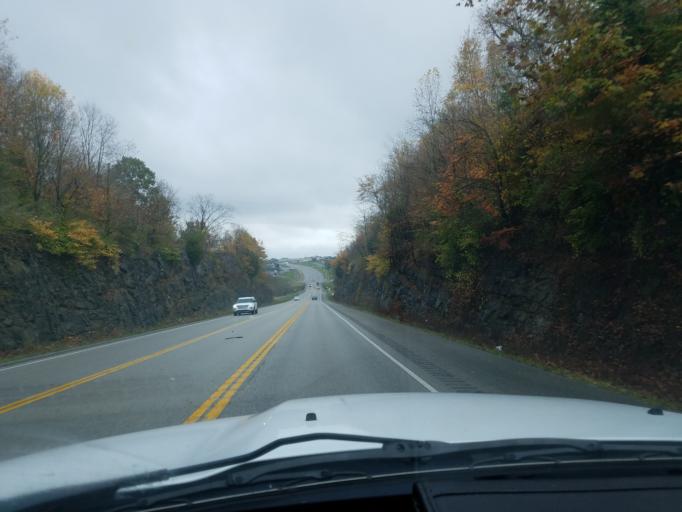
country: US
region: Kentucky
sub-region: Taylor County
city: Campbellsville
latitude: 37.3545
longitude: -85.3769
